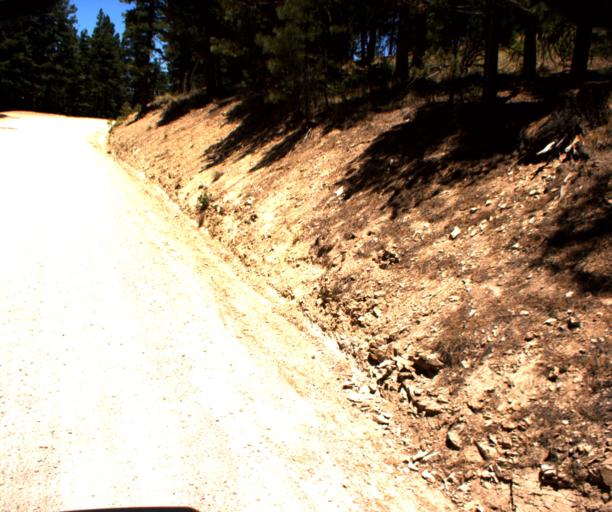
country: US
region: Arizona
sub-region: Graham County
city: Swift Trail Junction
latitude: 32.6600
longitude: -109.8655
